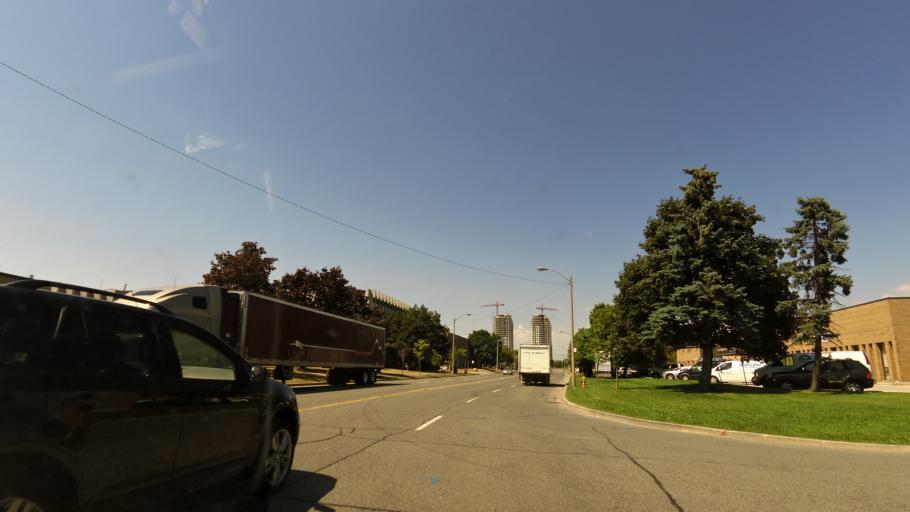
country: CA
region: Ontario
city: Etobicoke
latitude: 43.6151
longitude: -79.5179
